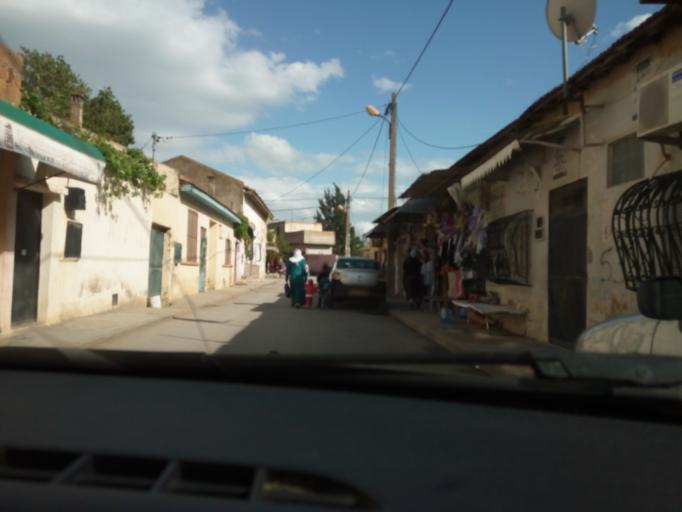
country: DZ
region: Tipaza
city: Hadjout
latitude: 36.3692
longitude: 2.4767
